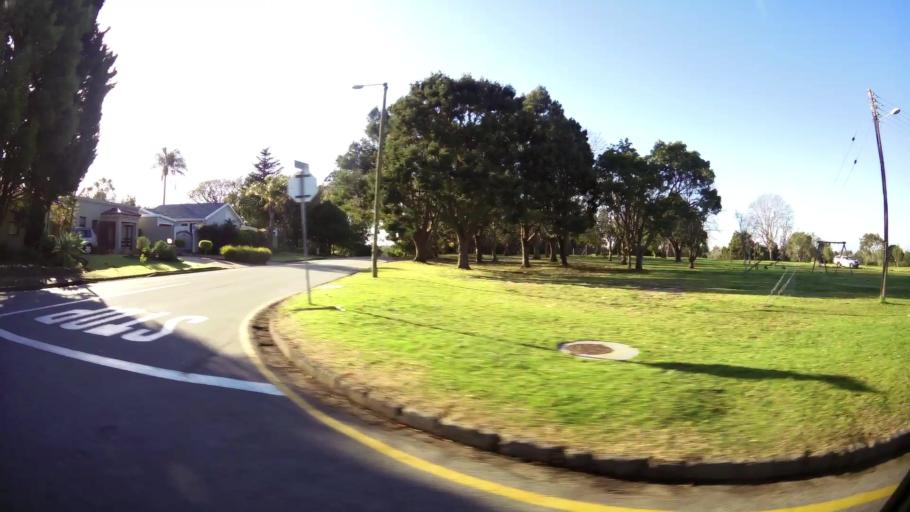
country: ZA
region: Western Cape
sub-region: Eden District Municipality
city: George
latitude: -33.9464
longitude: 22.4563
